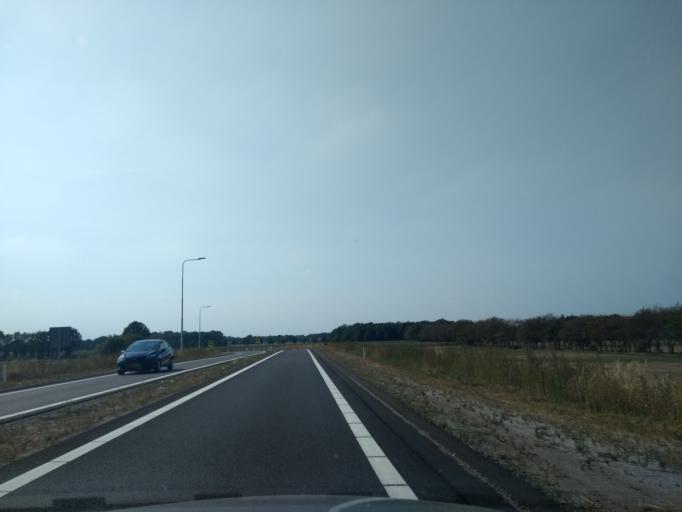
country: NL
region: Overijssel
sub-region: Gemeente Haaksbergen
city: Haaksbergen
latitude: 52.1829
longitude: 6.7582
